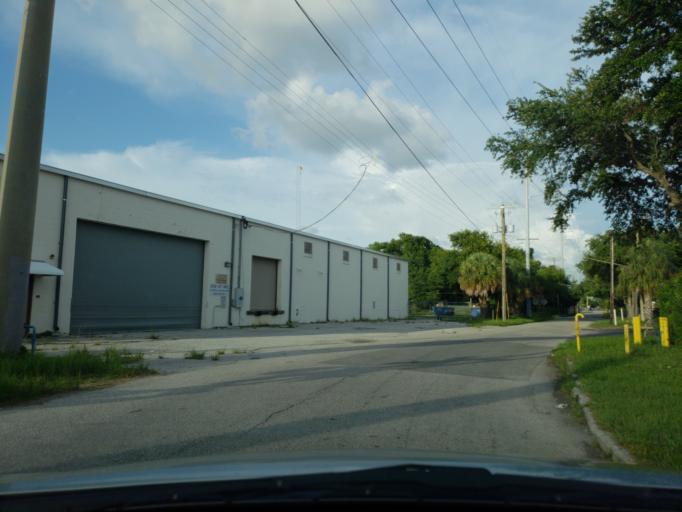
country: US
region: Florida
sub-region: Hillsborough County
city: Tampa
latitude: 27.9626
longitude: -82.4182
